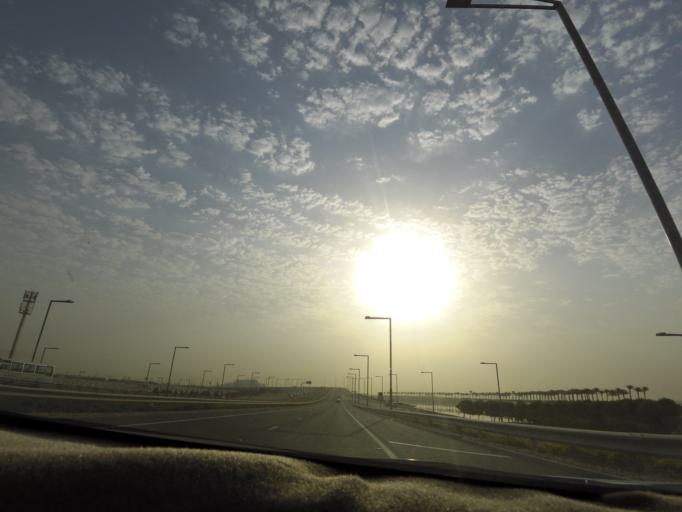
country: QA
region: Al Wakrah
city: Al Wakrah
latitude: 25.2489
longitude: 51.6133
